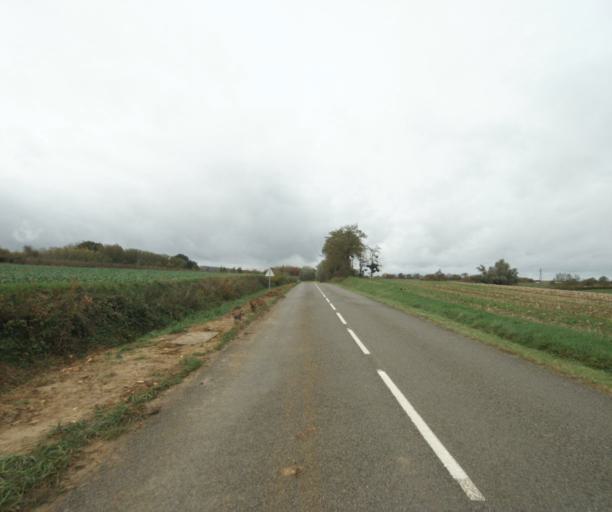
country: FR
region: Rhone-Alpes
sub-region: Departement de l'Ain
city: Pont-de-Vaux
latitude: 46.4589
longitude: 4.8827
